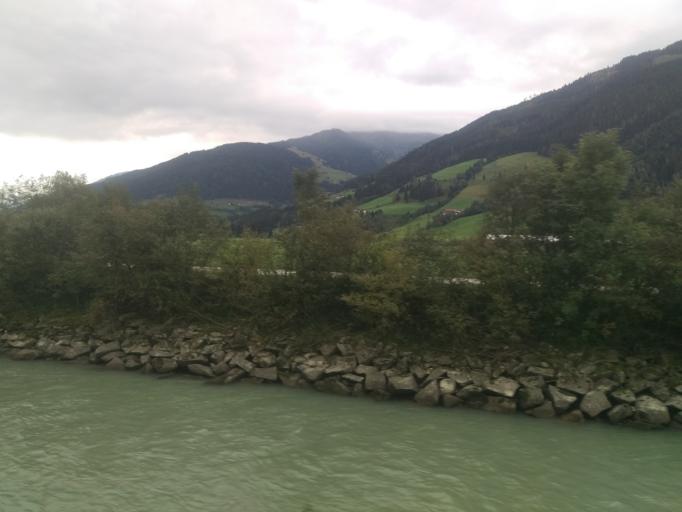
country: AT
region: Salzburg
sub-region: Politischer Bezirk Zell am See
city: Mittersill
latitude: 47.2825
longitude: 12.4518
